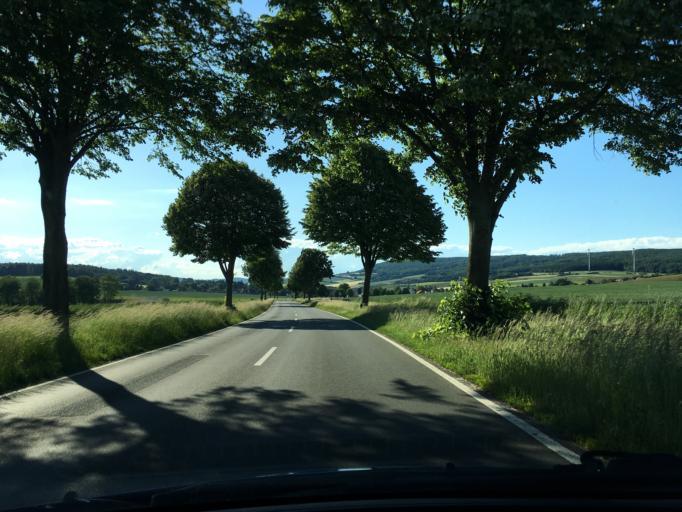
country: DE
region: Lower Saxony
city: Duingen
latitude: 52.0143
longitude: 9.6841
